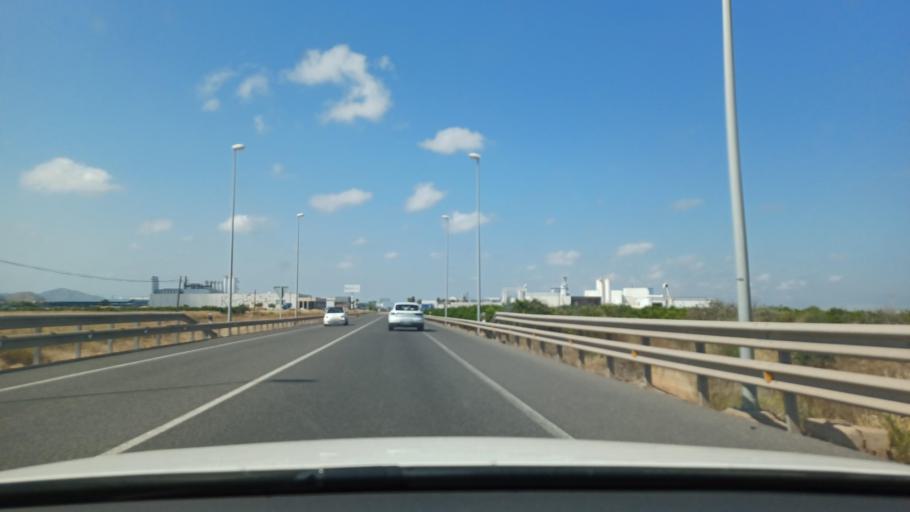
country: ES
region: Valencia
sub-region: Provincia de Castello
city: Moncofar
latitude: 39.8179
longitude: -0.1665
